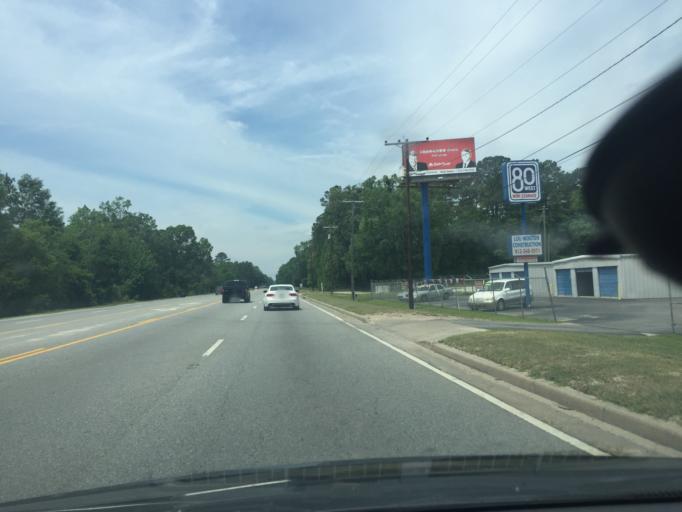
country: US
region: Georgia
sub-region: Chatham County
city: Bloomingdale
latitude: 32.1245
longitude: -81.2741
